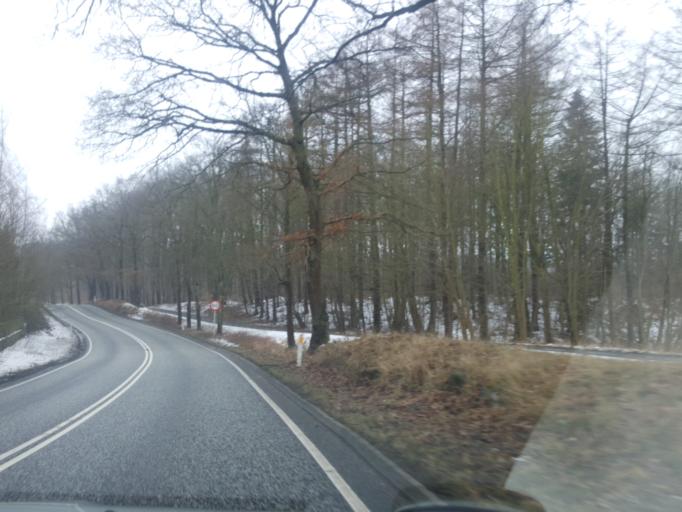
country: DK
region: Capital Region
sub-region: Horsholm Kommune
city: Horsholm
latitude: 55.8650
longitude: 12.4713
